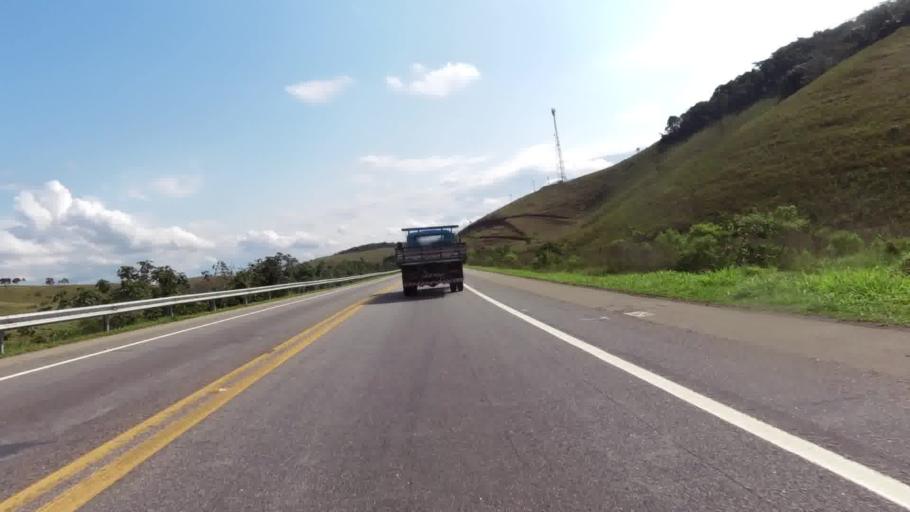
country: BR
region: Rio de Janeiro
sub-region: Macae
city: Macae
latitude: -22.2435
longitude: -41.8031
